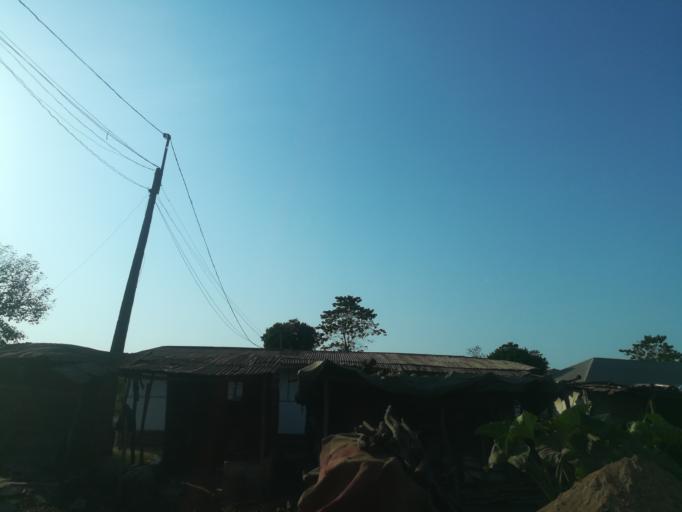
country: NG
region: Ogun
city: Abeokuta
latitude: 7.1870
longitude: 3.2825
